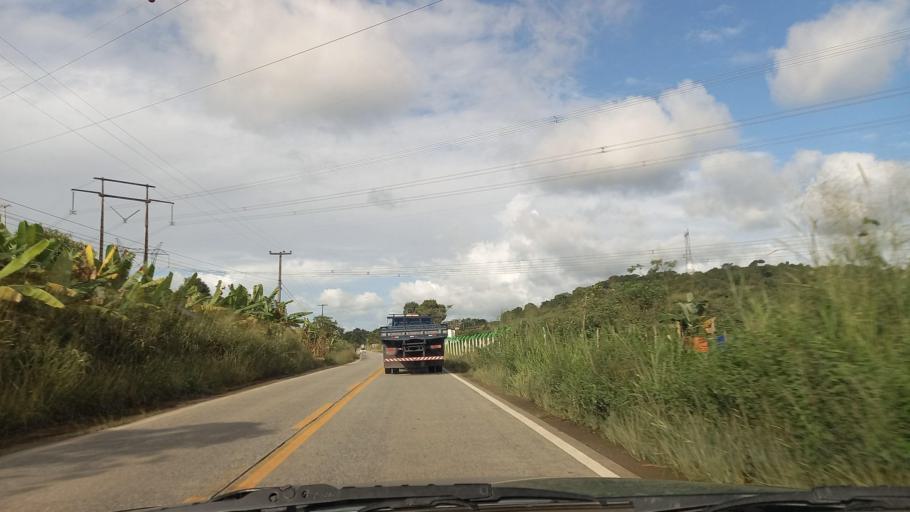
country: BR
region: Pernambuco
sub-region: Palmares
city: Palmares
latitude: -8.6912
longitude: -35.6165
